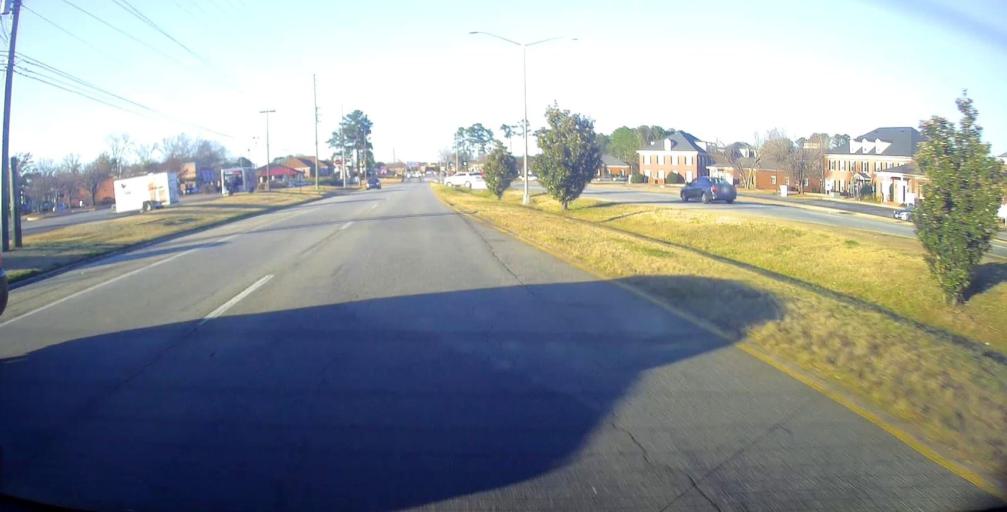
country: US
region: Georgia
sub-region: Dougherty County
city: Albany
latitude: 31.6119
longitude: -84.2232
